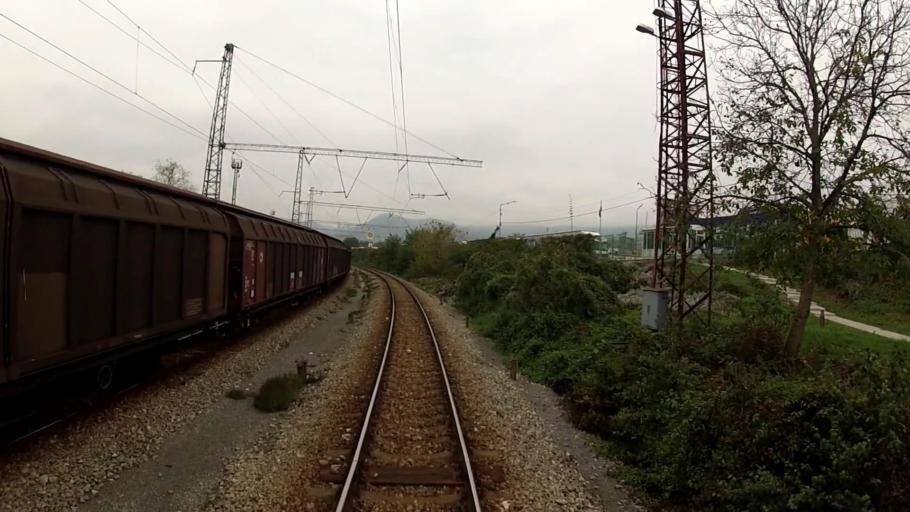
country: RS
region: Central Serbia
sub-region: Pirotski Okrug
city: Dimitrovgrad
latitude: 42.9933
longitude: 22.8464
